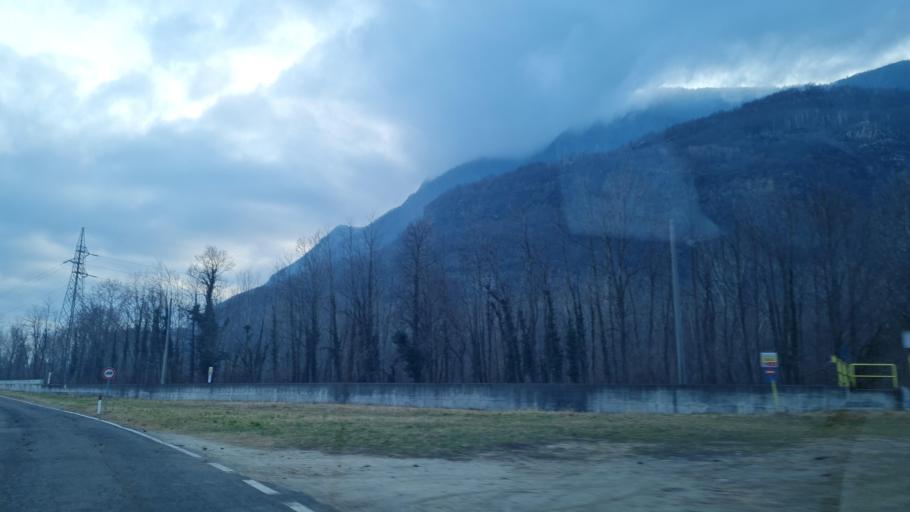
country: IT
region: Piedmont
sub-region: Provincia di Torino
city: Quassolo
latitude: 45.5351
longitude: 7.8357
